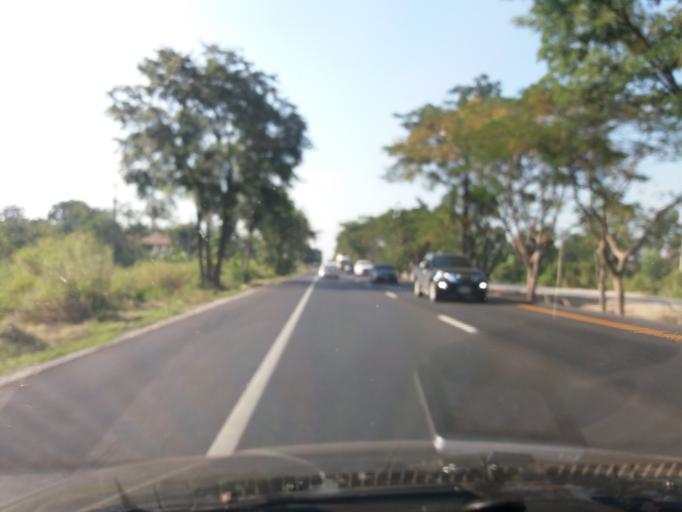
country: TH
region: Nakhon Sawan
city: Kao Liao
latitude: 15.7788
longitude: 99.9770
